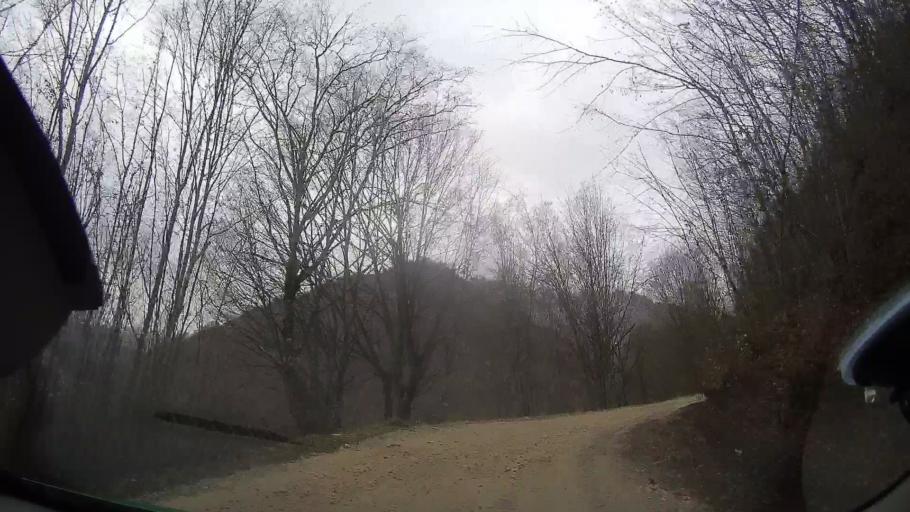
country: RO
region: Cluj
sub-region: Comuna Maguri-Racatau
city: Maguri-Racatau
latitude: 46.6512
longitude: 23.1976
